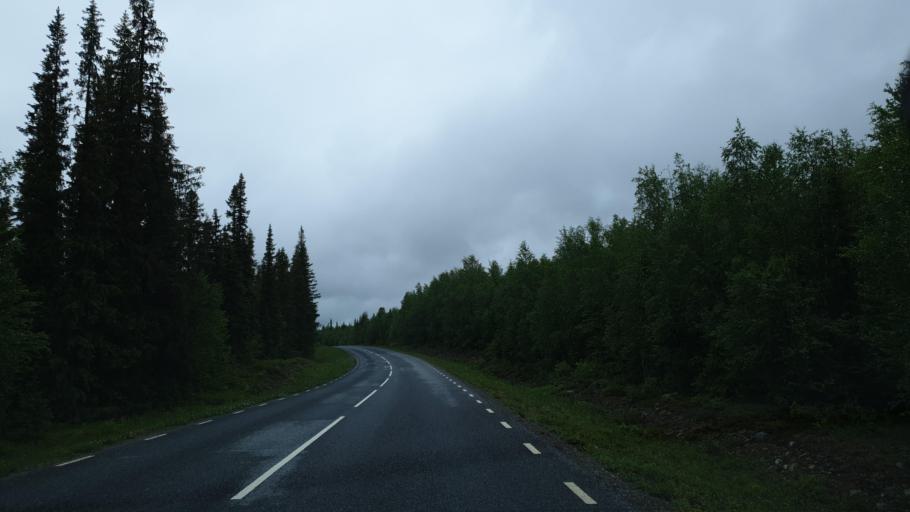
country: SE
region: Vaesterbotten
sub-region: Vilhelmina Kommun
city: Sjoberg
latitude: 65.2294
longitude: 15.8799
